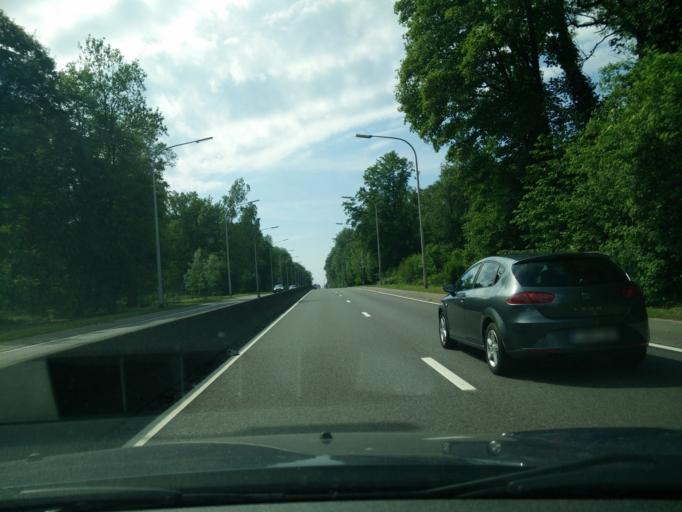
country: BE
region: Wallonia
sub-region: Province du Hainaut
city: Gerpinnes
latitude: 50.3522
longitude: 4.4715
